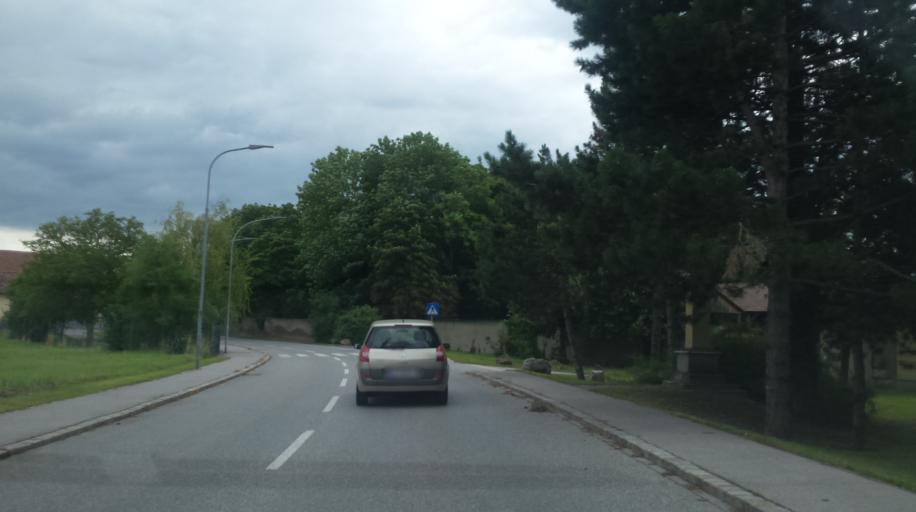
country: AT
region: Lower Austria
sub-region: Politischer Bezirk Wien-Umgebung
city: Zwolfaxing
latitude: 48.1113
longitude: 16.4600
